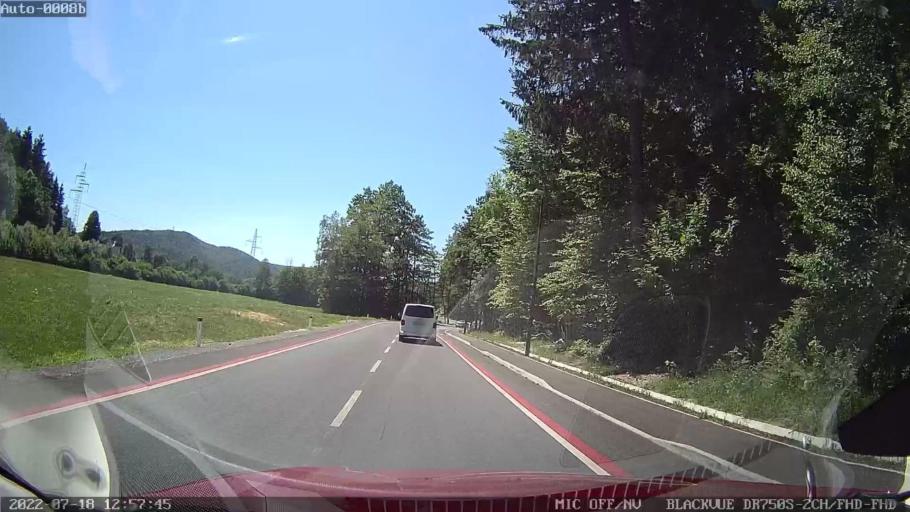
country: SI
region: Dobrova-Horjul-Polhov Gradec
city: Dobrova
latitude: 46.0665
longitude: 14.4217
